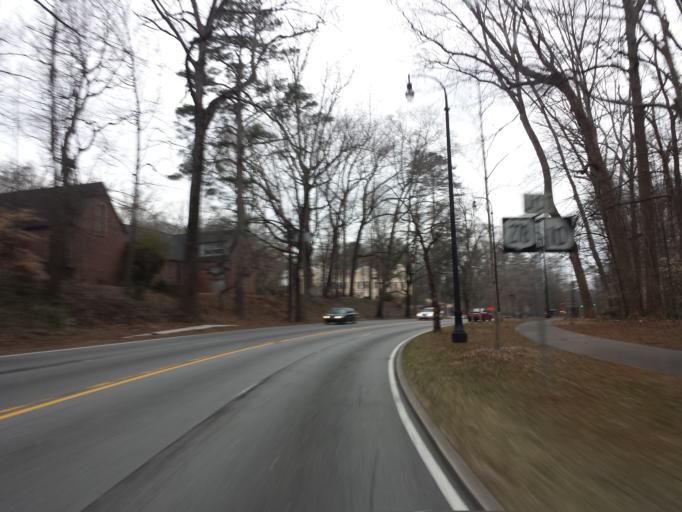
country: US
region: Georgia
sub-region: DeKalb County
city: Druid Hills
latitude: 33.7713
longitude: -84.3189
